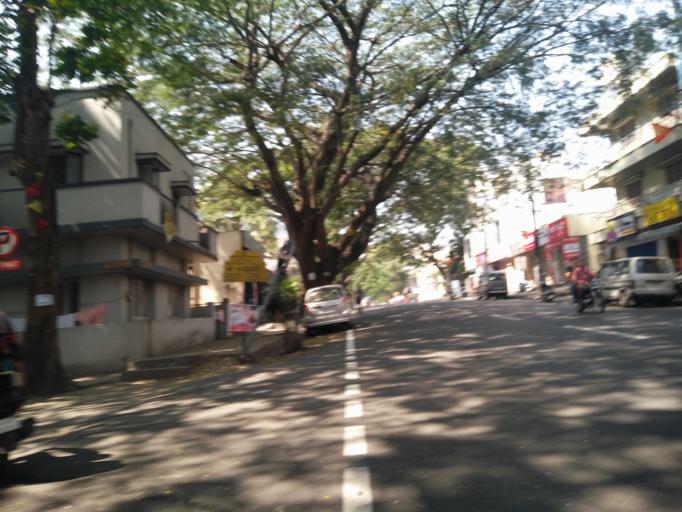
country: IN
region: Karnataka
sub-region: Bangalore Urban
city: Bangalore
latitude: 12.9681
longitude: 77.5389
